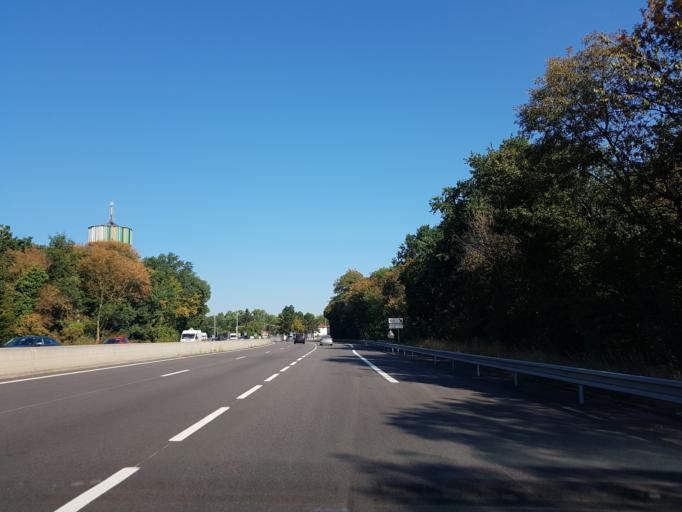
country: FR
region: Alsace
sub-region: Departement du Haut-Rhin
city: Kingersheim
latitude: 47.7797
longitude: 7.3318
